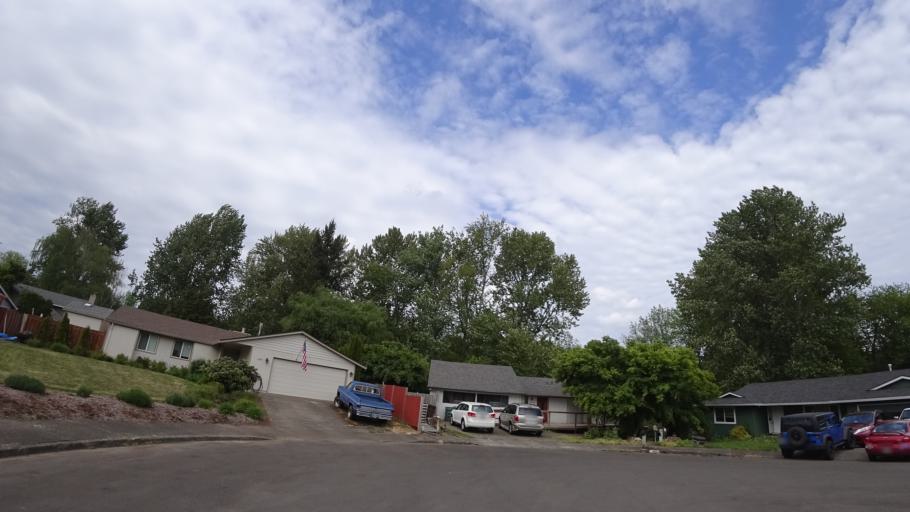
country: US
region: Oregon
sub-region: Washington County
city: Hillsboro
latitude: 45.4945
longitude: -122.9521
